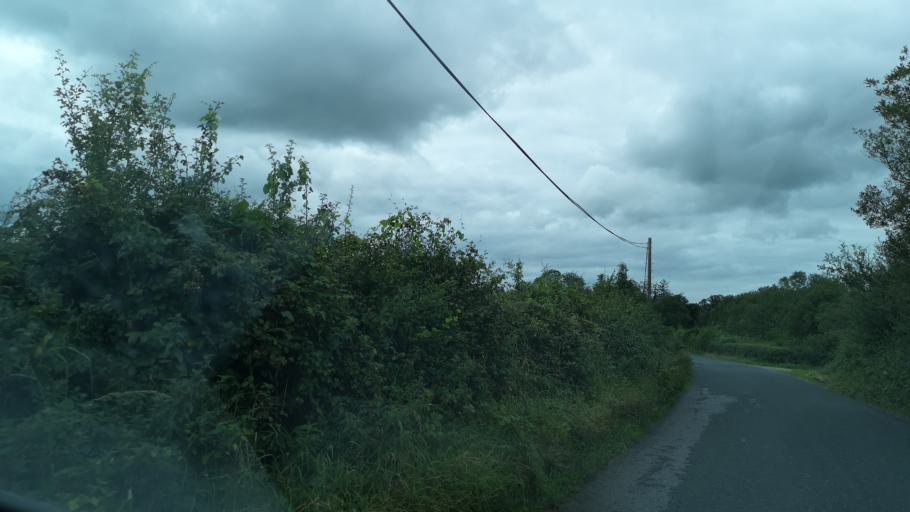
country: IE
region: Connaught
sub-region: County Galway
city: Loughrea
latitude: 53.1622
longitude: -8.4649
